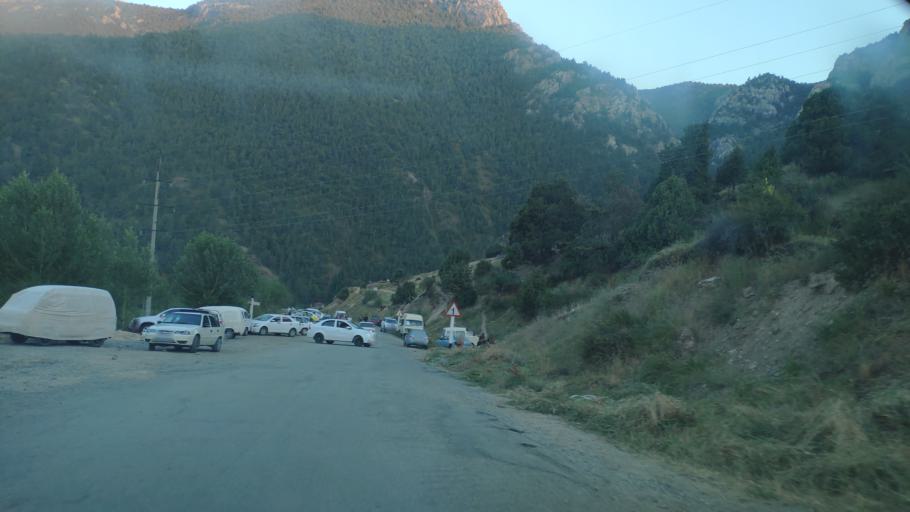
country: TJ
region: Viloyati Sughd
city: Ayni
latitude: 39.6337
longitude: 68.4909
